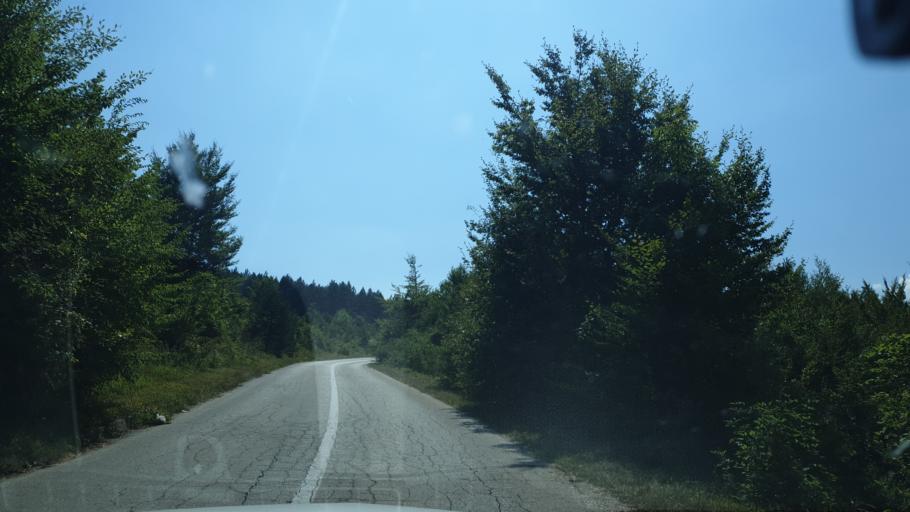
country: RS
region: Central Serbia
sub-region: Zlatiborski Okrug
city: Cajetina
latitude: 43.6789
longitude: 19.8510
